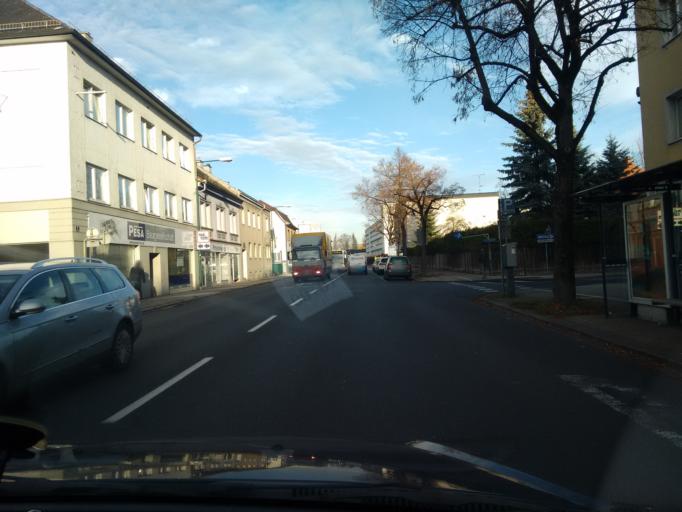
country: AT
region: Upper Austria
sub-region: Wels Stadt
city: Wels
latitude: 48.1592
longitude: 14.0199
